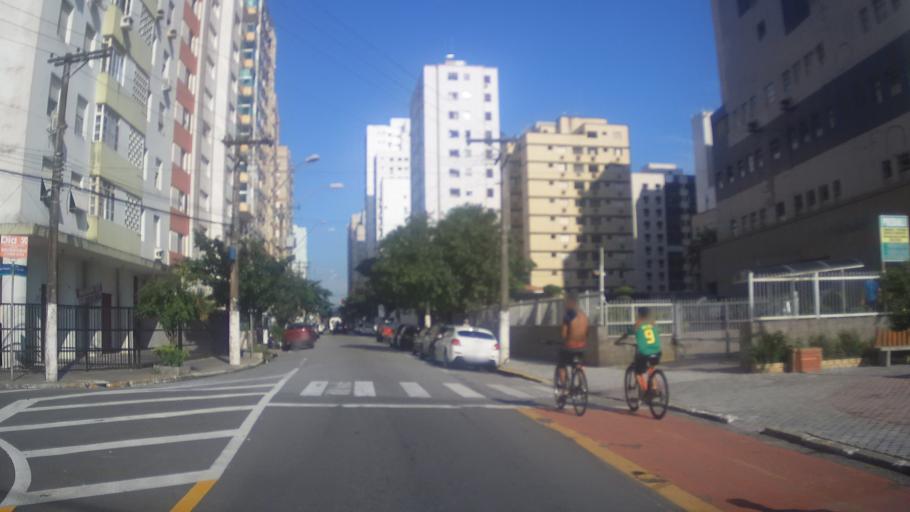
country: BR
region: Sao Paulo
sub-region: Sao Vicente
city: Sao Vicente
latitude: -23.9710
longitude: -46.3737
